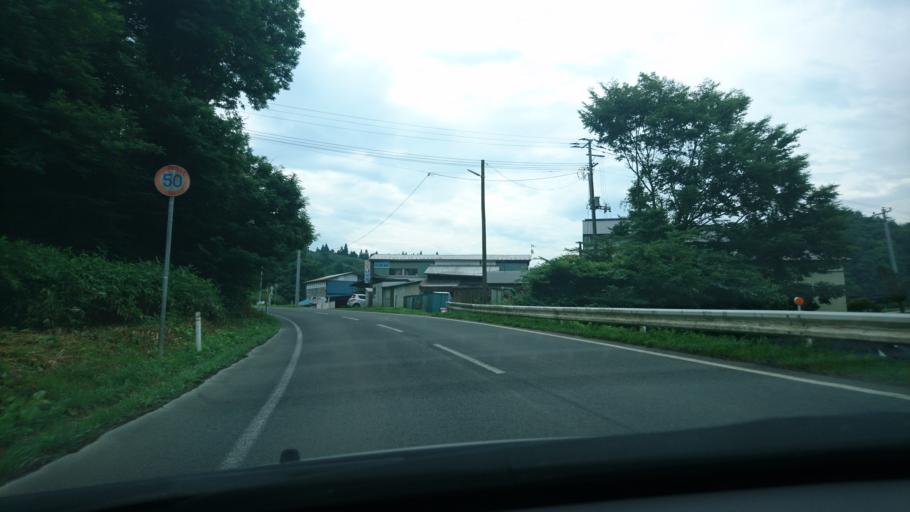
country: JP
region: Iwate
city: Ichinoseki
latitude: 38.9183
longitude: 141.4198
